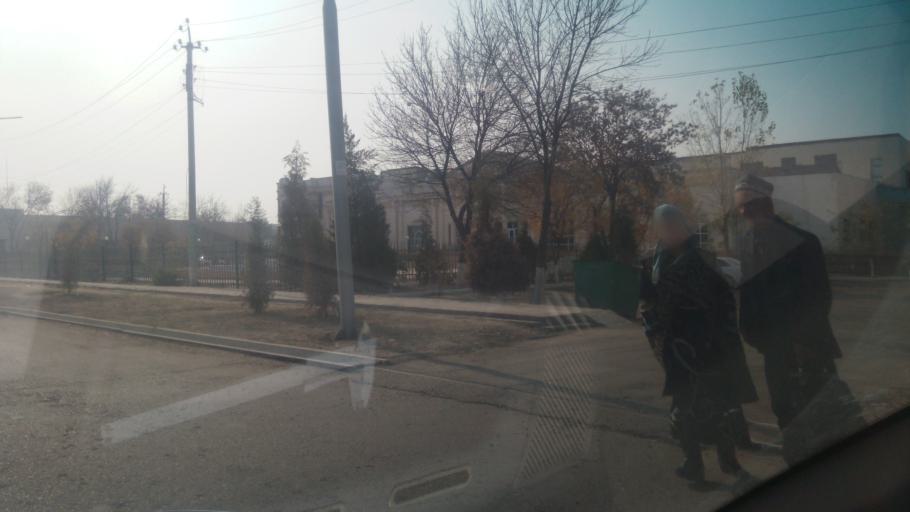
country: UZ
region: Sirdaryo
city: Guliston
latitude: 40.5078
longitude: 68.7735
